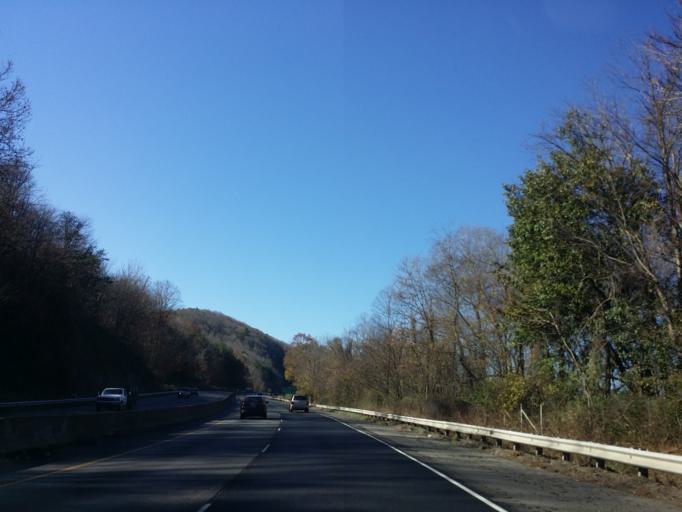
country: US
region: North Carolina
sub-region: Buncombe County
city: Biltmore Forest
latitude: 35.5753
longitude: -82.4792
